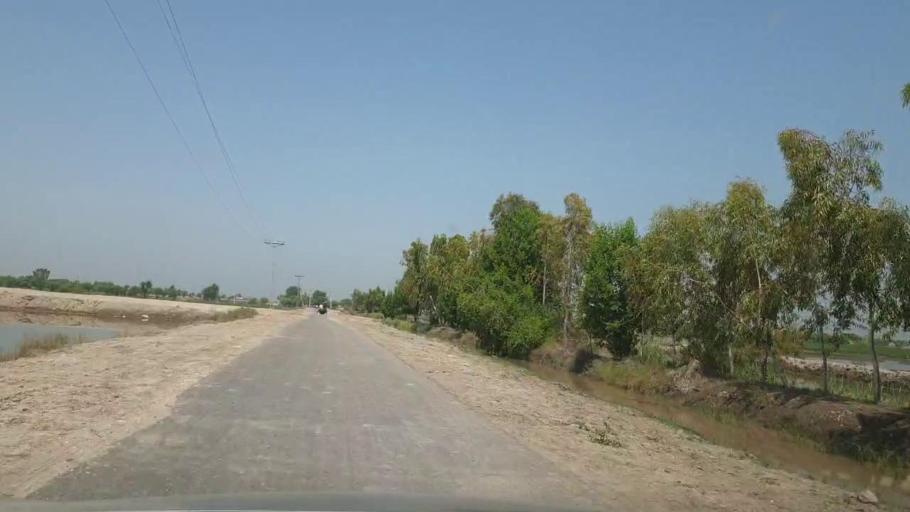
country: PK
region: Sindh
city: Warah
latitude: 27.4764
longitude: 67.7579
